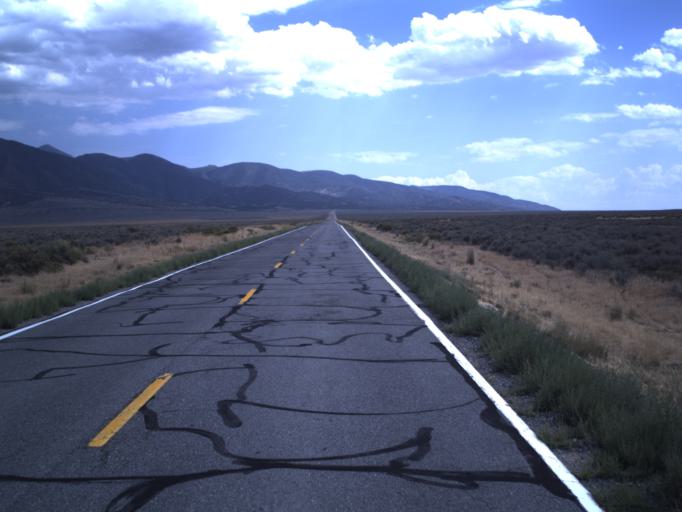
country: US
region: Utah
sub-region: Tooele County
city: Tooele
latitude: 40.3778
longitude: -112.3779
